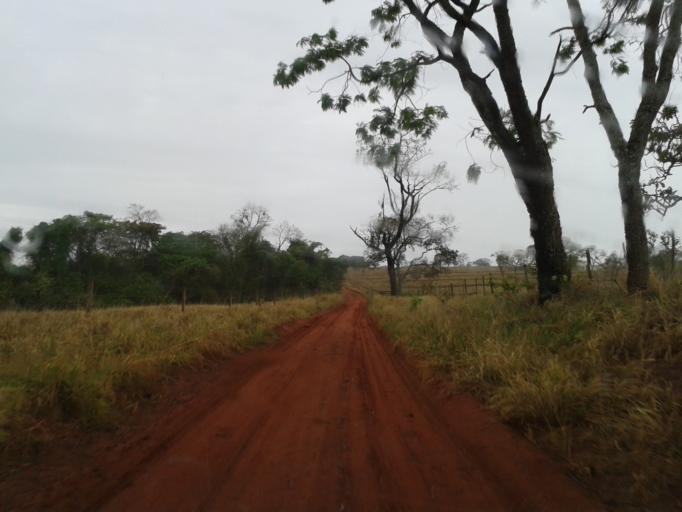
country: BR
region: Minas Gerais
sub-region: Campina Verde
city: Campina Verde
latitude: -19.3545
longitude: -49.5377
